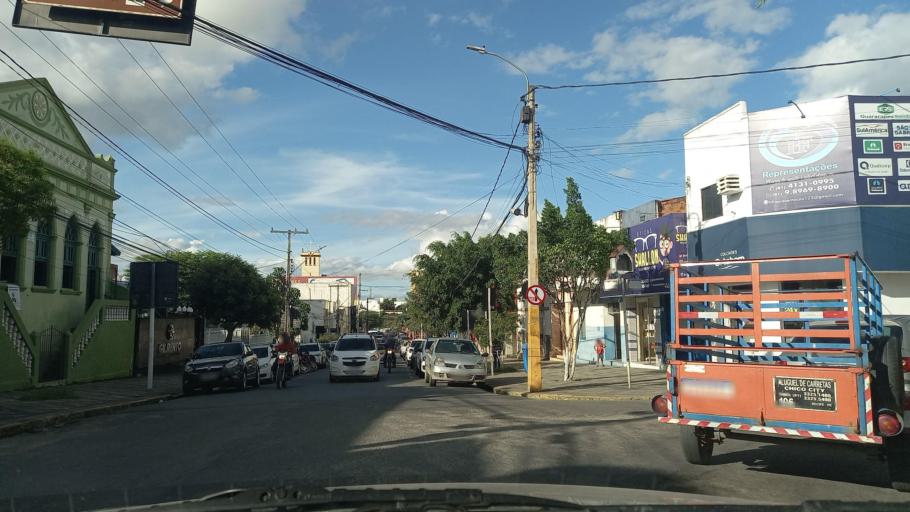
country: BR
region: Pernambuco
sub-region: Gravata
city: Gravata
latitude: -8.2044
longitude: -35.5694
